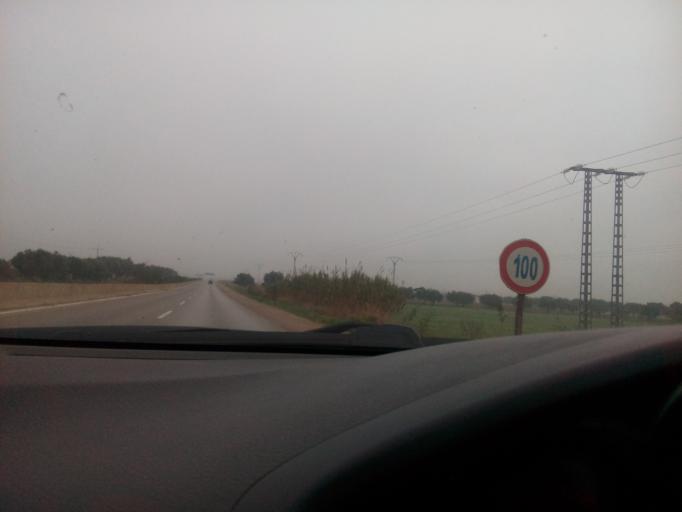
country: DZ
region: Oran
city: Bou Tlelis
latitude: 35.5640
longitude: -0.9224
